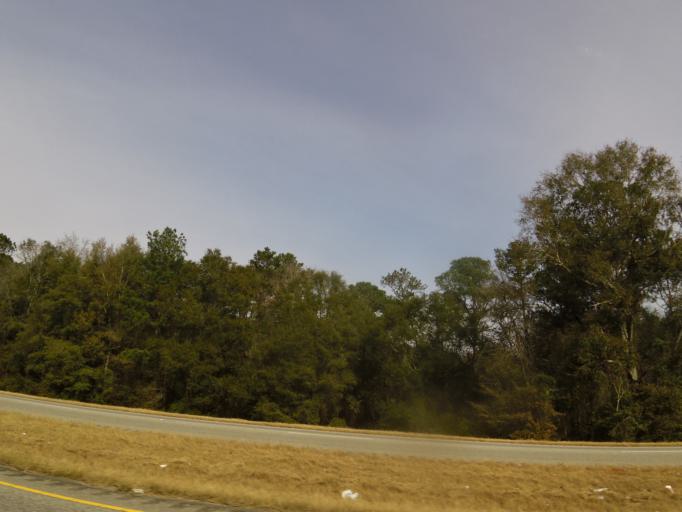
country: US
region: Alabama
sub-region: Dale County
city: Midland City
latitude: 31.3054
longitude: -85.4926
